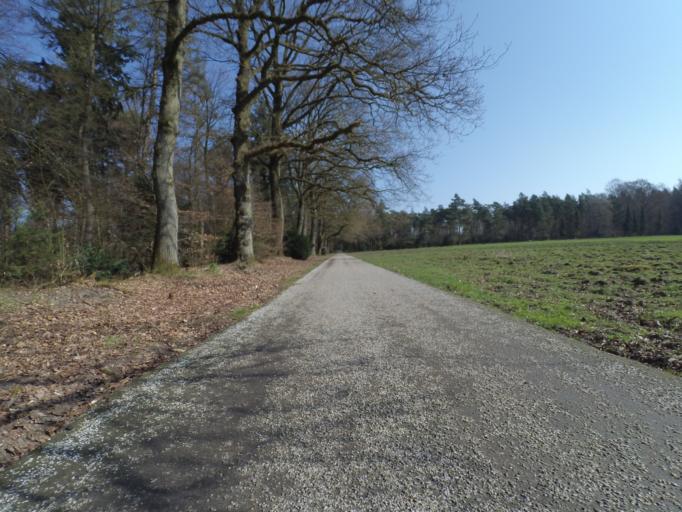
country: NL
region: Gelderland
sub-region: Gemeente Ede
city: Otterlo
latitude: 52.1028
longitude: 5.8390
